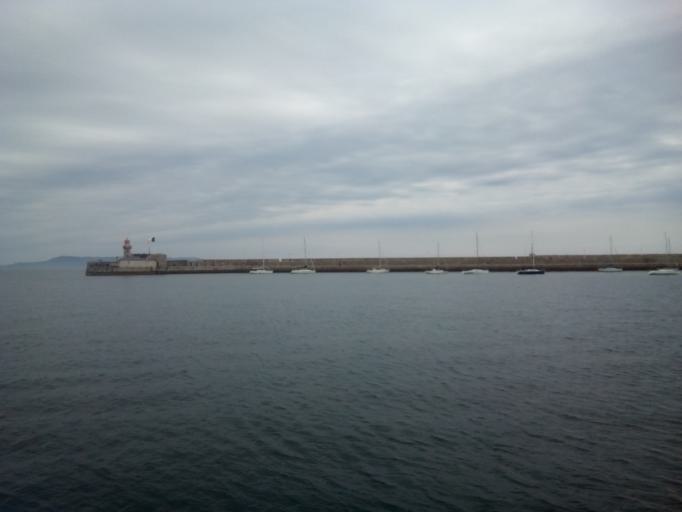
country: IE
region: Leinster
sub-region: Dun Laoghaire-Rathdown
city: Dun Laoghaire
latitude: 53.2998
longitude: -6.1293
